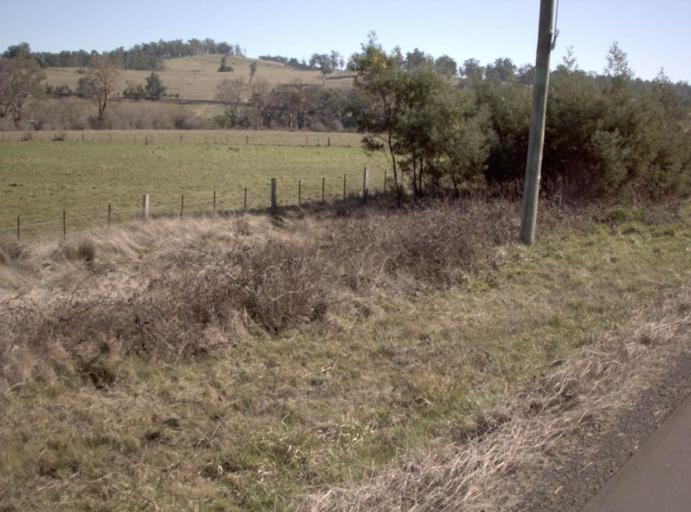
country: AU
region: Tasmania
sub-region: Launceston
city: Mayfield
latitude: -41.3137
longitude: 147.0531
